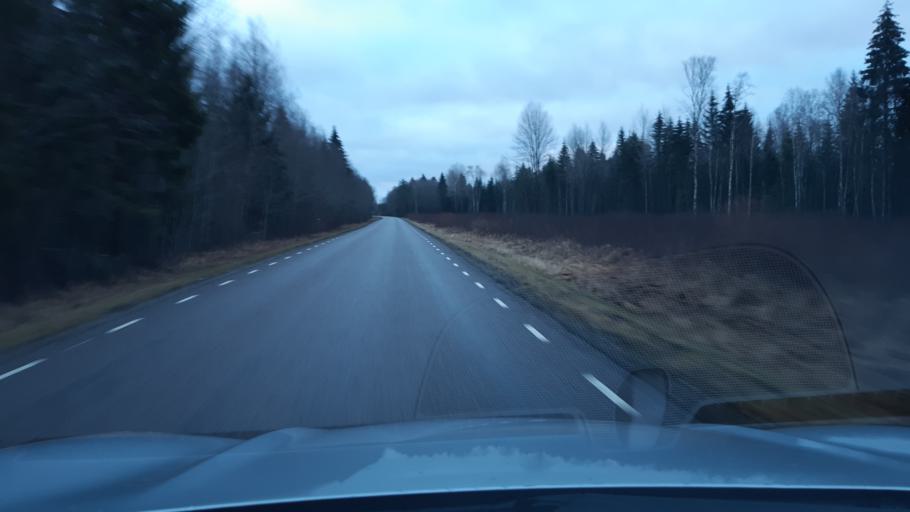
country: EE
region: Raplamaa
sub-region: Kohila vald
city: Kohila
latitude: 59.1346
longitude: 24.6615
